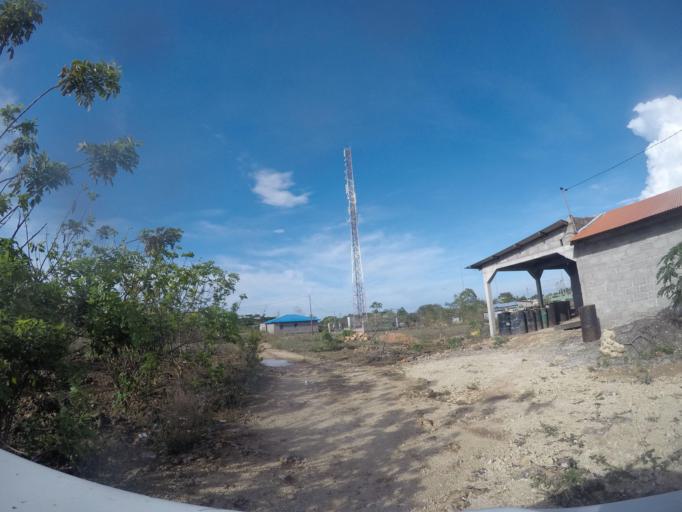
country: TL
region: Baucau
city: Baucau
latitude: -8.4880
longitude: 126.4534
